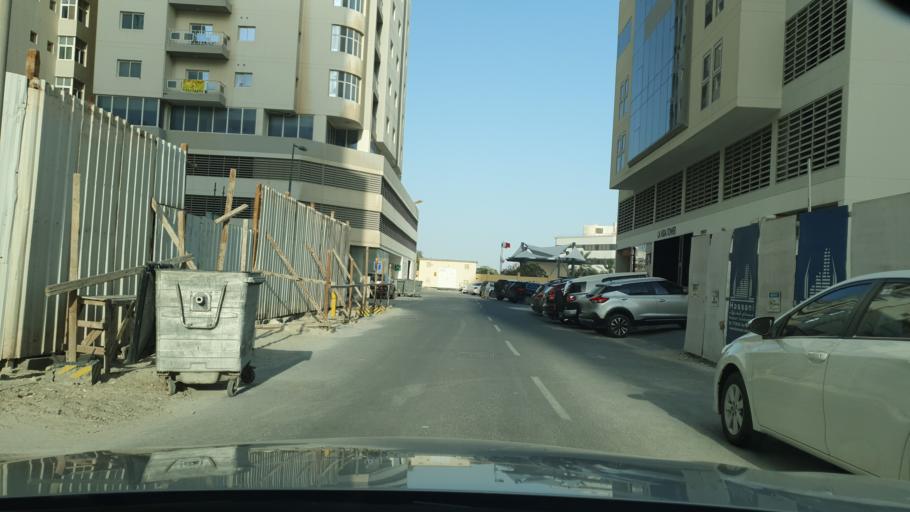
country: BH
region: Muharraq
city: Al Muharraq
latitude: 26.2635
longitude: 50.5969
